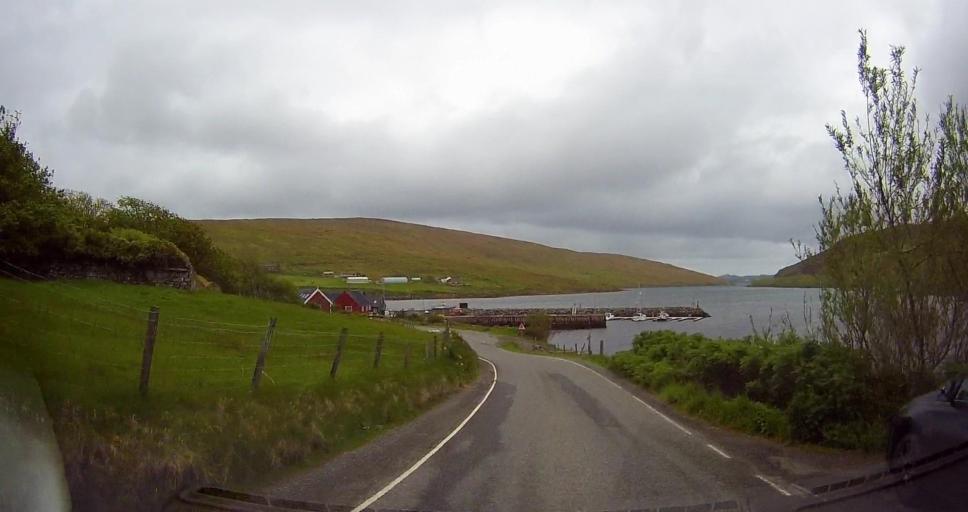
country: GB
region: Scotland
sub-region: Shetland Islands
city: Lerwick
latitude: 60.3506
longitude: -1.2623
